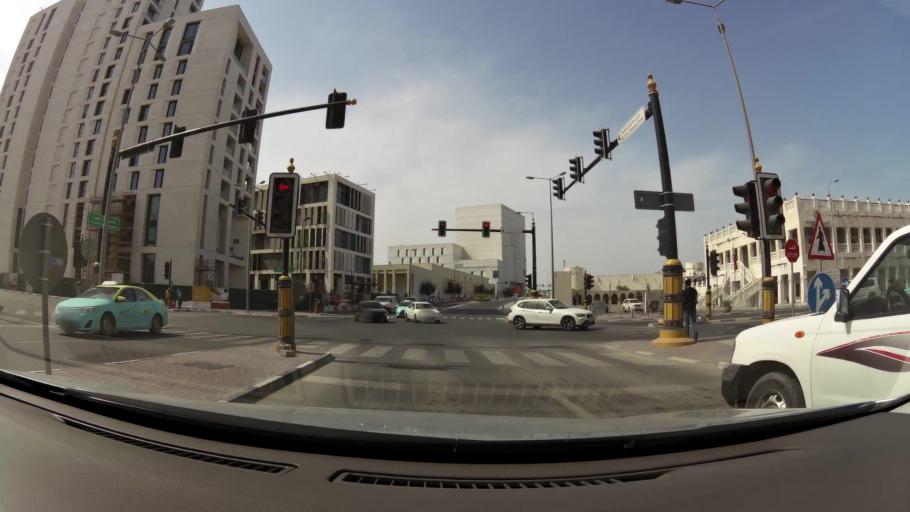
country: QA
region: Baladiyat ad Dawhah
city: Doha
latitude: 25.2854
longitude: 51.5312
